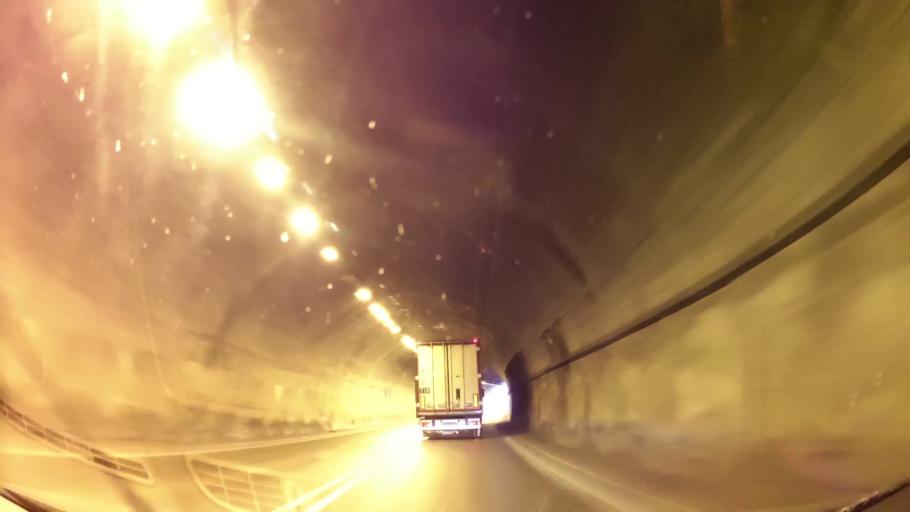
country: RS
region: Central Serbia
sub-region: Pcinjski Okrug
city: Vladicin Han
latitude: 42.7498
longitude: 22.0659
